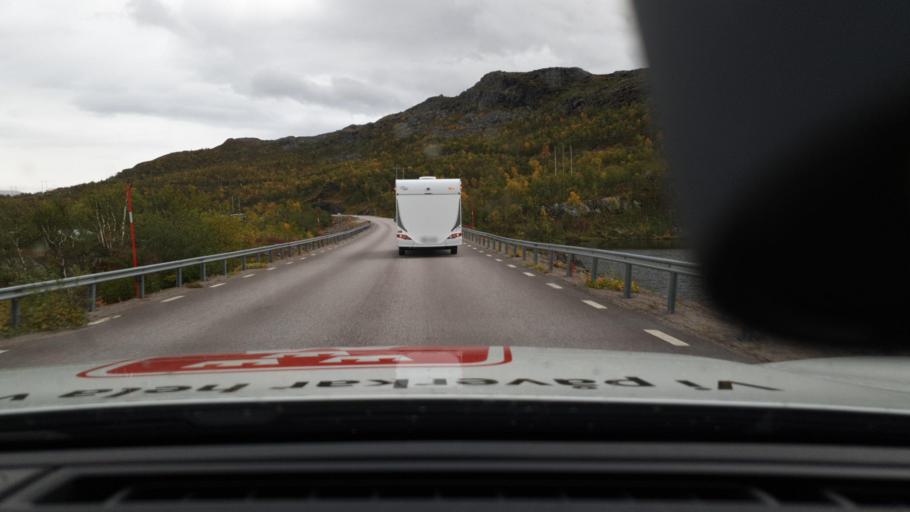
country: NO
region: Troms
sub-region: Bardu
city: Setermoen
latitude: 68.4308
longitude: 18.5460
